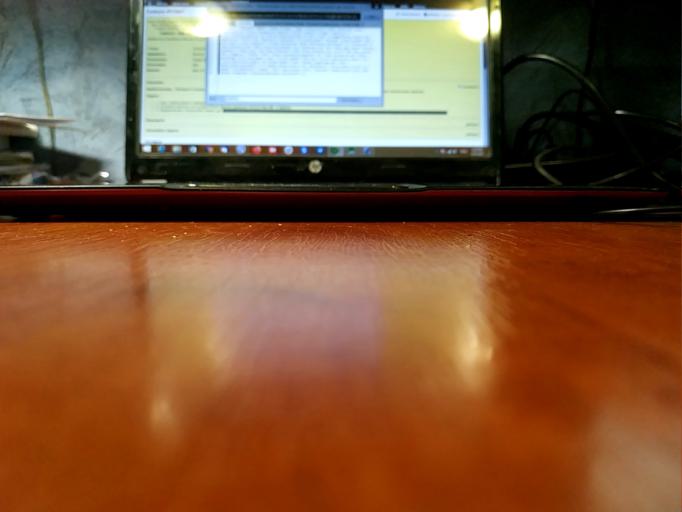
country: RU
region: Tverskaya
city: Sandovo
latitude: 58.4878
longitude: 36.3765
